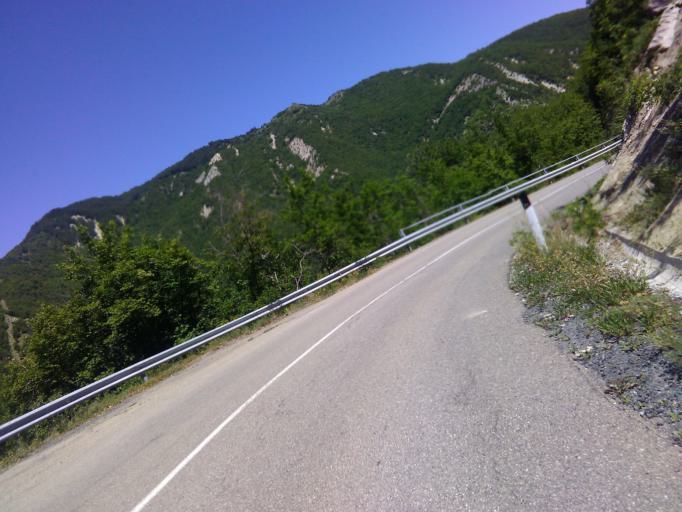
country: IT
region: Emilia-Romagna
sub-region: Provincia di Parma
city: Terenzo
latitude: 44.5846
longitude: 10.0903
